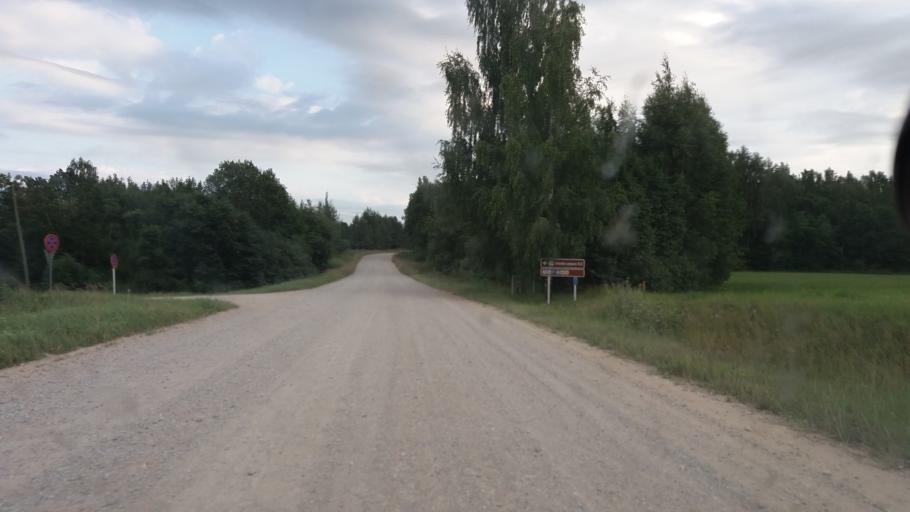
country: LV
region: Talsu Rajons
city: Sabile
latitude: 57.0225
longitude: 22.5868
